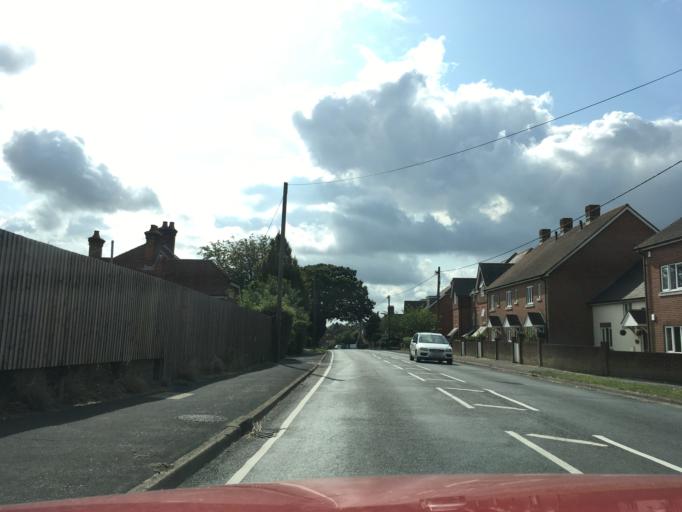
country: GB
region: England
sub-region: Hampshire
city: Bishops Waltham
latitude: 50.9571
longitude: -1.2257
